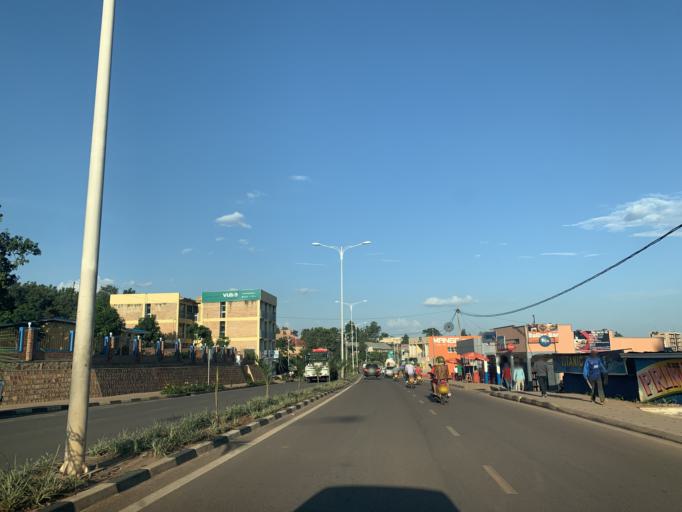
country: RW
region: Kigali
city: Kigali
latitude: -1.9603
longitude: 30.1154
